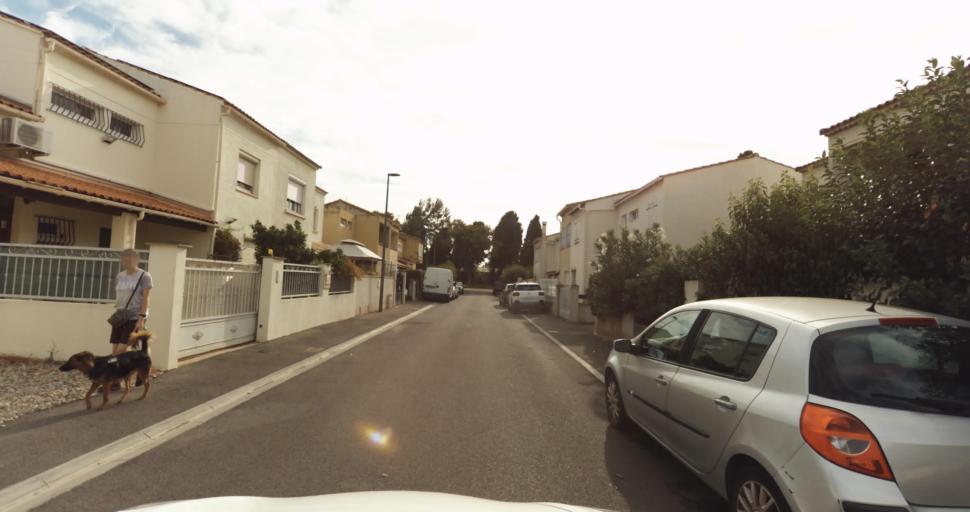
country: FR
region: Provence-Alpes-Cote d'Azur
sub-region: Departement des Bouches-du-Rhone
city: Miramas
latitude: 43.5895
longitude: 4.9974
